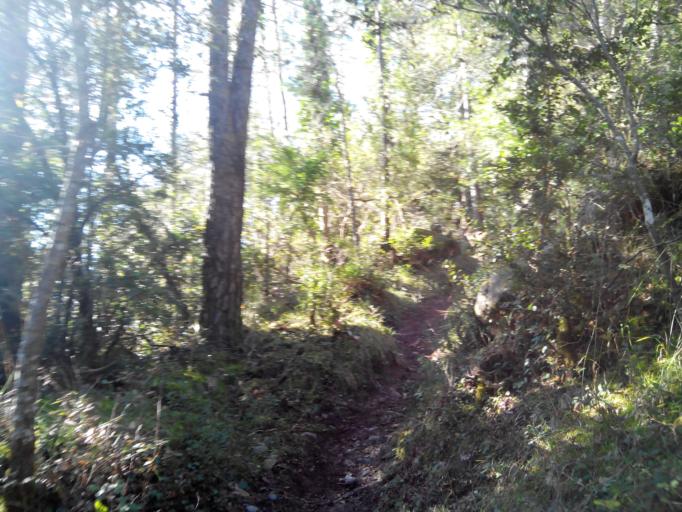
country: ES
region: Catalonia
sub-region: Provincia de Barcelona
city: Vilada
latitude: 42.1074
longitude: 1.9317
